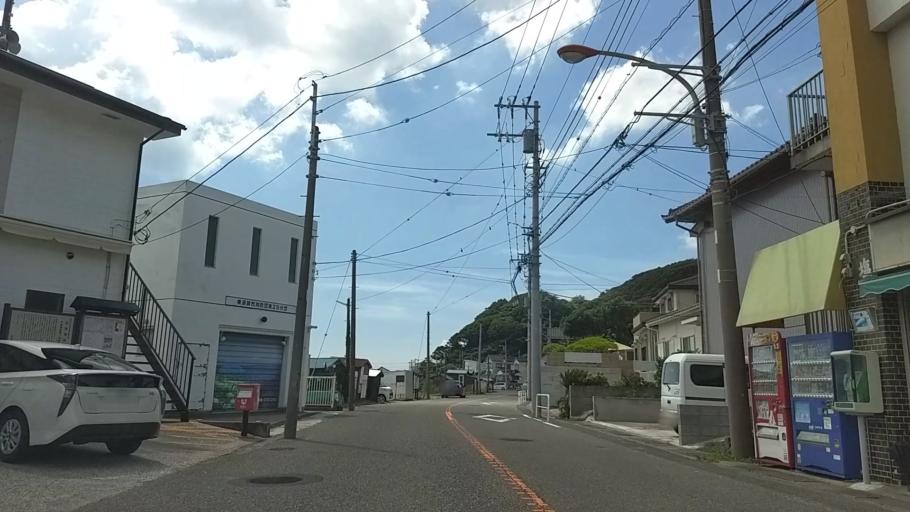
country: JP
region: Kanagawa
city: Hayama
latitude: 35.2237
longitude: 139.6089
